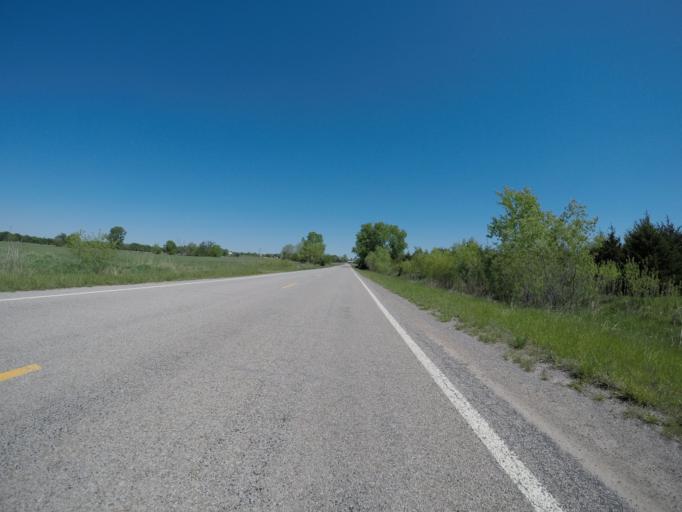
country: US
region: Kansas
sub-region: Osage County
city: Overbrook
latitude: 38.9006
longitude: -95.5285
